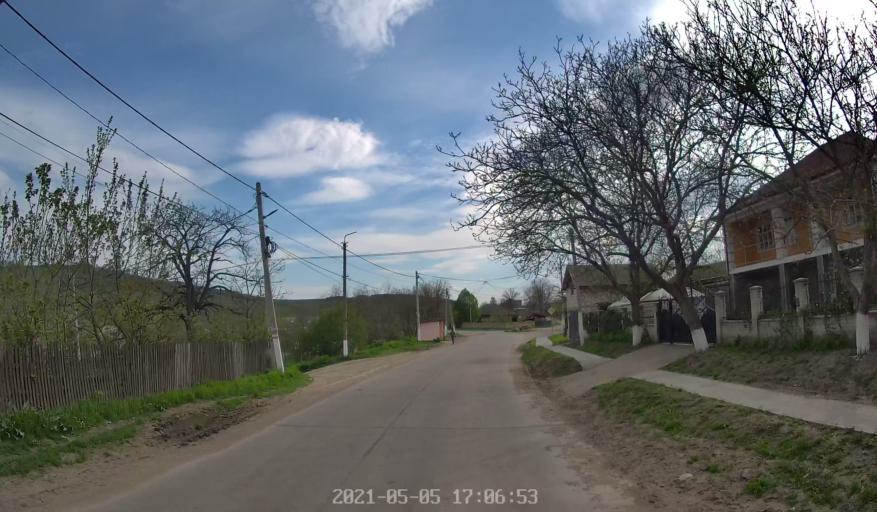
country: MD
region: Chisinau
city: Vadul lui Voda
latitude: 47.0167
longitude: 29.1376
